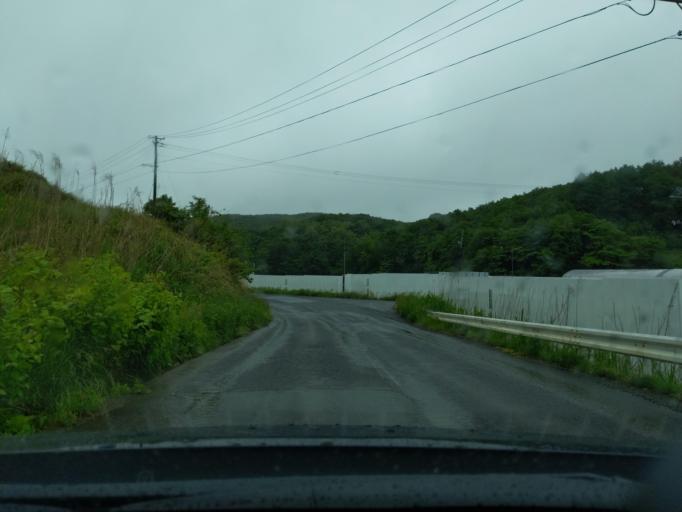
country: JP
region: Fukushima
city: Funehikimachi-funehiki
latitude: 37.6015
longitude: 140.6390
